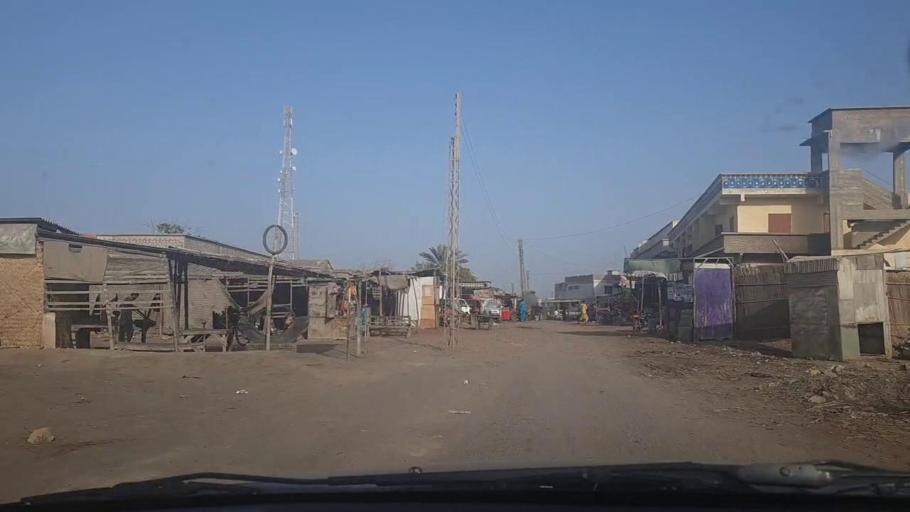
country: PK
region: Sindh
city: Keti Bandar
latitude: 24.3009
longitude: 67.6034
